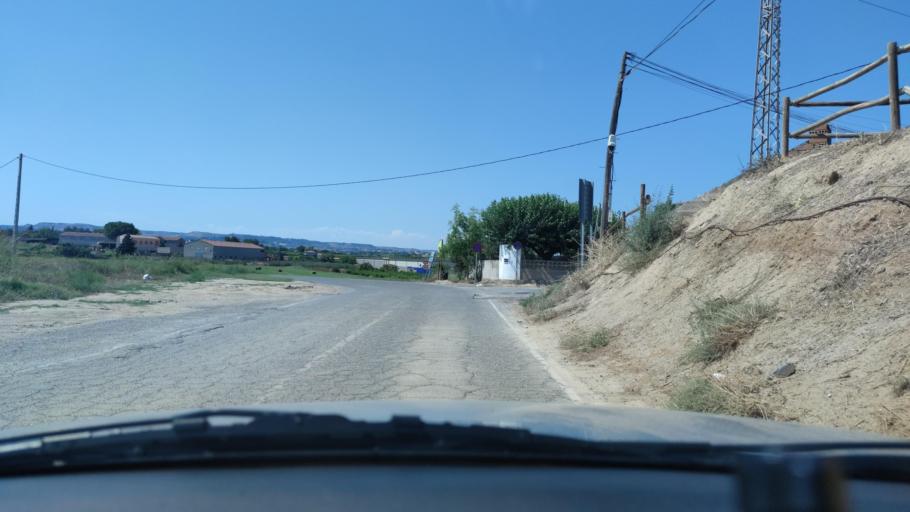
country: ES
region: Catalonia
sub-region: Provincia de Lleida
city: Lleida
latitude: 41.6425
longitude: 0.6241
